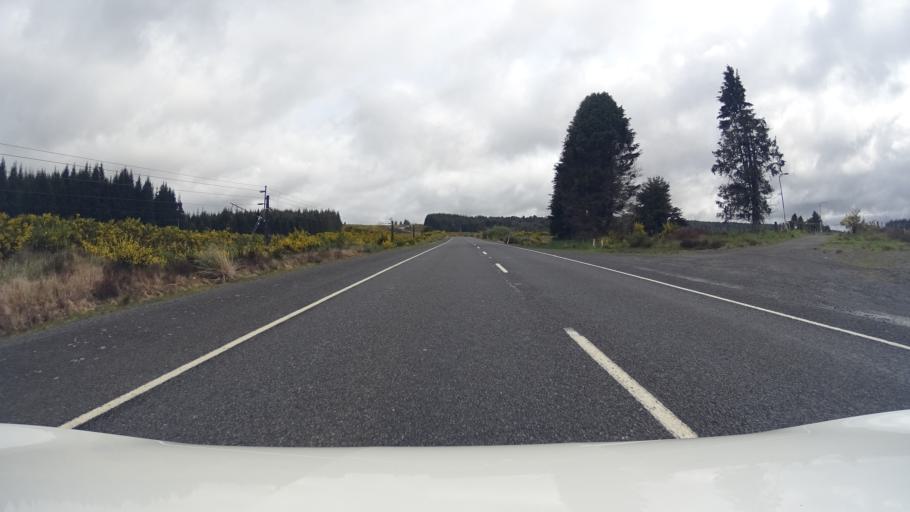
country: NZ
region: Manawatu-Wanganui
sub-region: Ruapehu District
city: Waiouru
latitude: -39.2093
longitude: 175.4023
